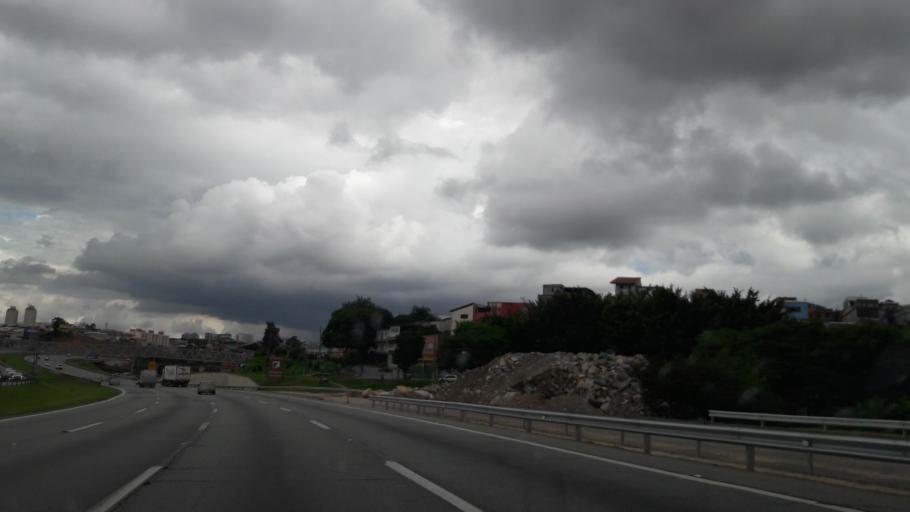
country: BR
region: Sao Paulo
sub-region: Osasco
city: Osasco
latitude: -23.5667
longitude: -46.8187
